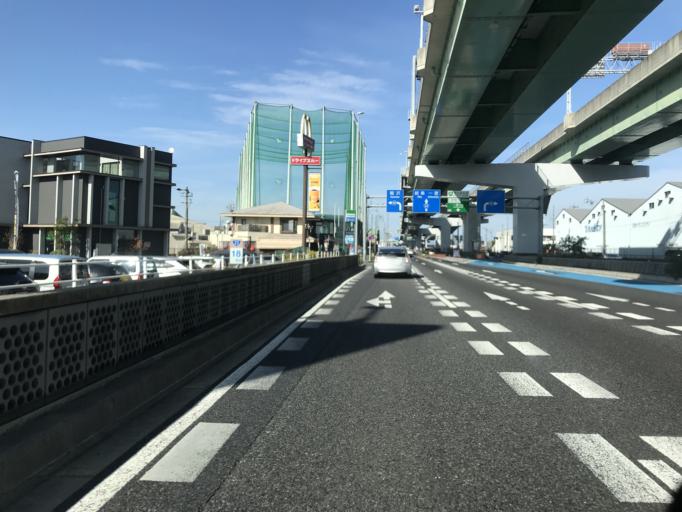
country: JP
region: Aichi
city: Iwakura
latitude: 35.2558
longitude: 136.8428
